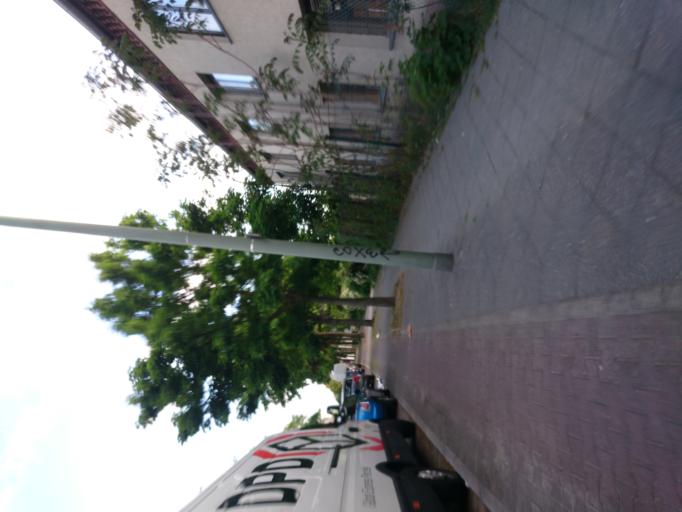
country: DE
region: Berlin
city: Wittenau
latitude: 52.5760
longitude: 13.3136
